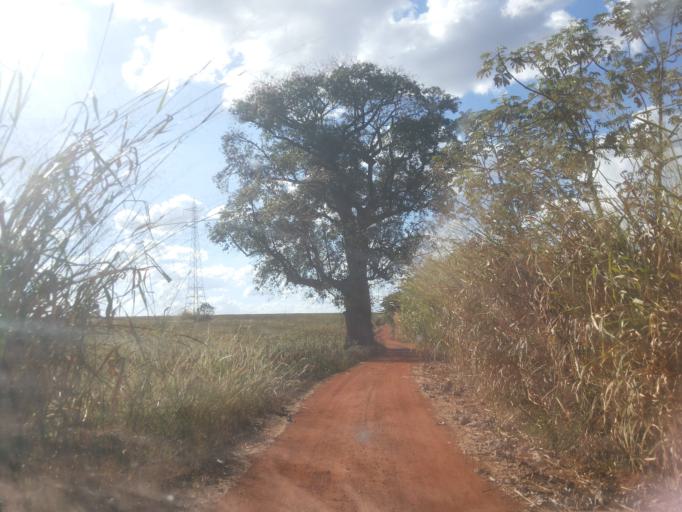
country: BR
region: Minas Gerais
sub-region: Capinopolis
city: Capinopolis
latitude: -18.5947
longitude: -49.4952
